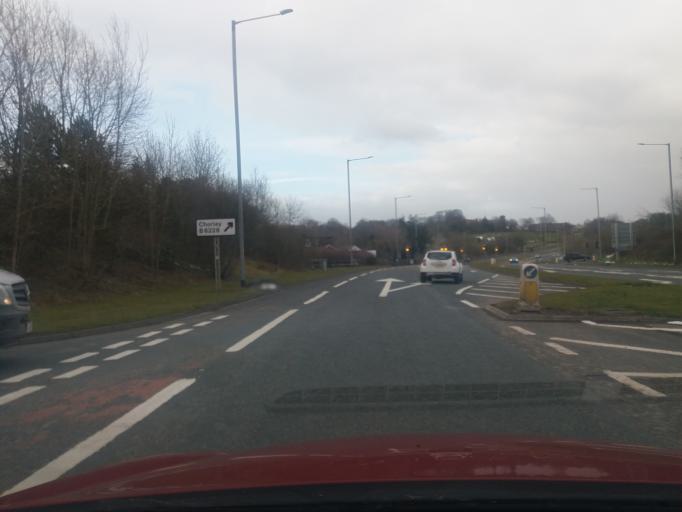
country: GB
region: England
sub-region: Lancashire
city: Chorley
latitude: 53.6781
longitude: -2.6178
